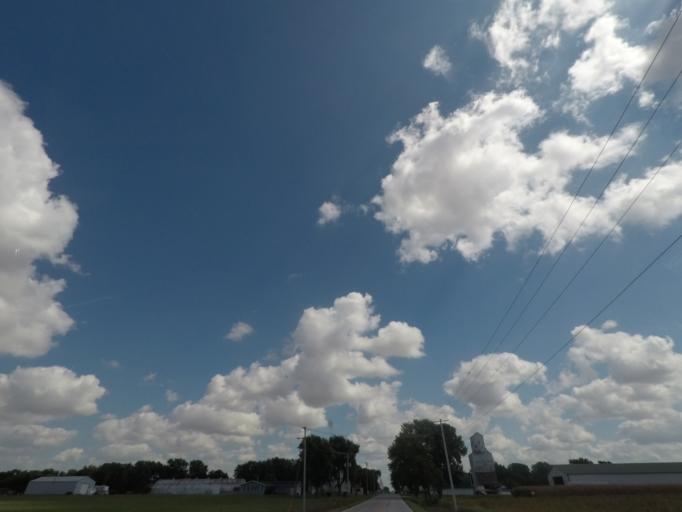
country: US
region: Iowa
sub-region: Story County
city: Nevada
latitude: 42.0706
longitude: -93.3988
